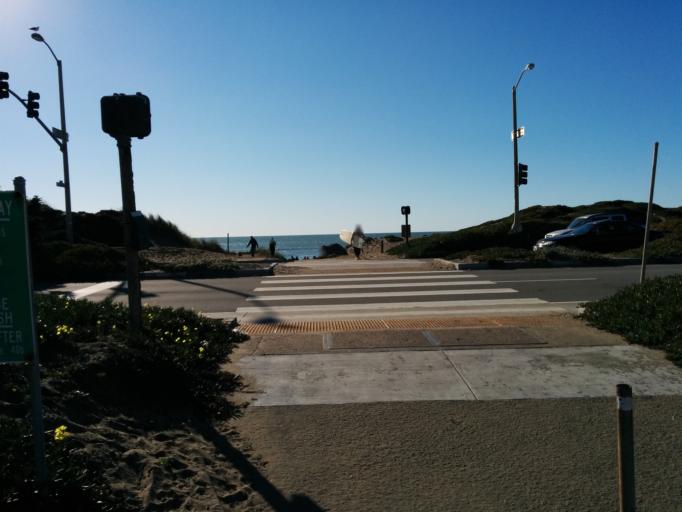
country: US
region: California
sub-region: San Mateo County
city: Daly City
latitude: 37.7417
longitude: -122.5073
